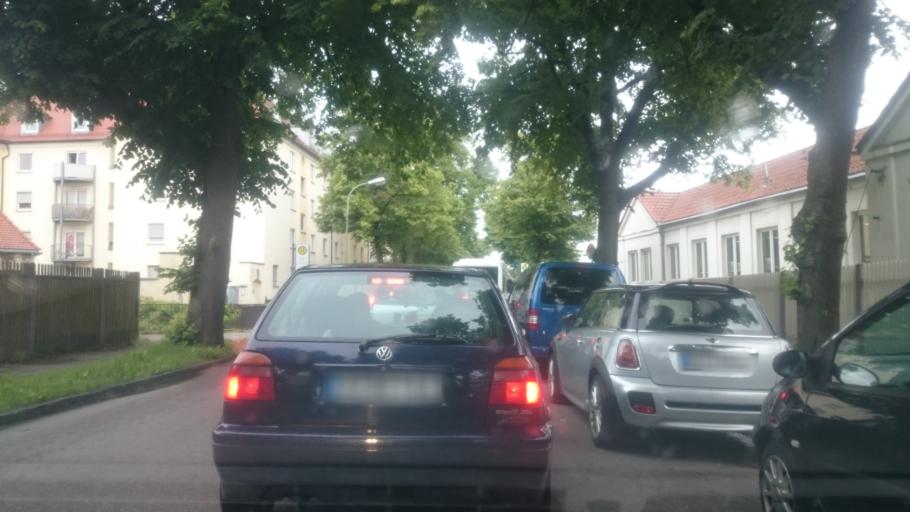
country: DE
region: Bavaria
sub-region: Swabia
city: Augsburg
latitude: 48.3679
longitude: 10.9141
